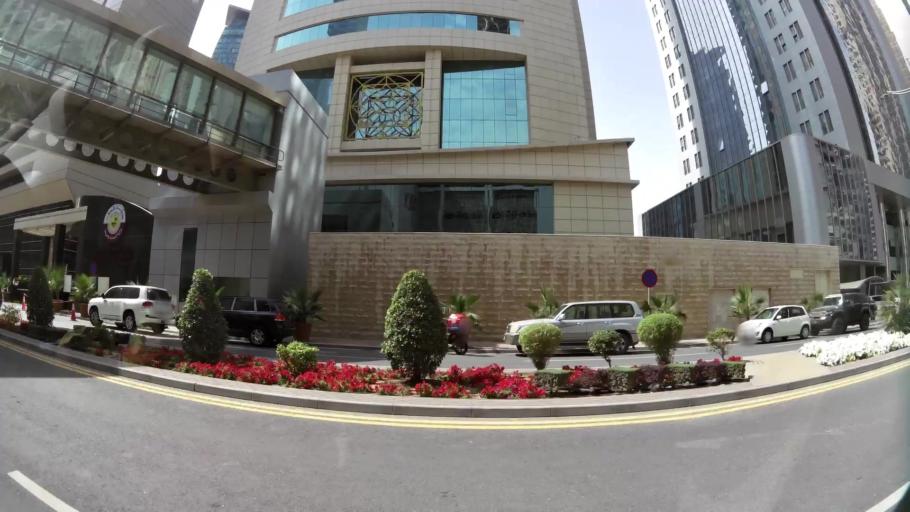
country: QA
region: Baladiyat ad Dawhah
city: Doha
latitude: 25.3265
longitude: 51.5342
